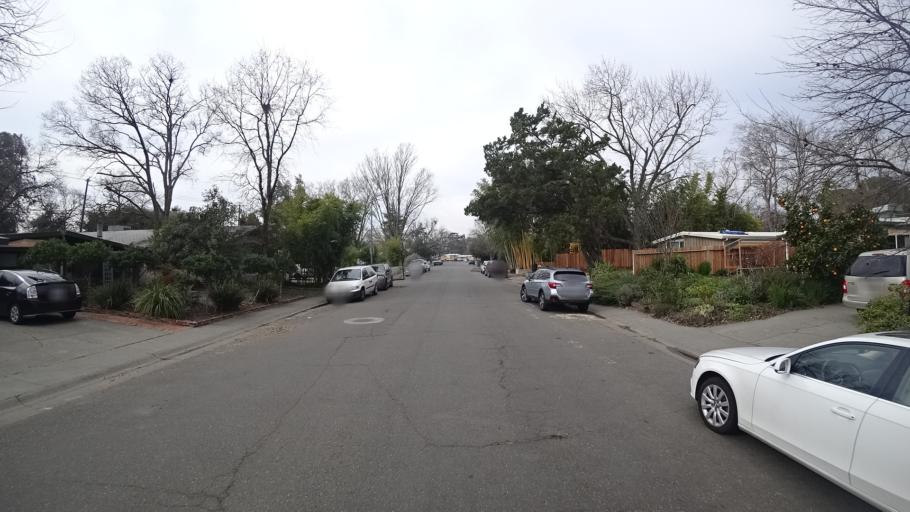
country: US
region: California
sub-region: Yolo County
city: Davis
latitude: 38.5502
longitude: -121.7329
